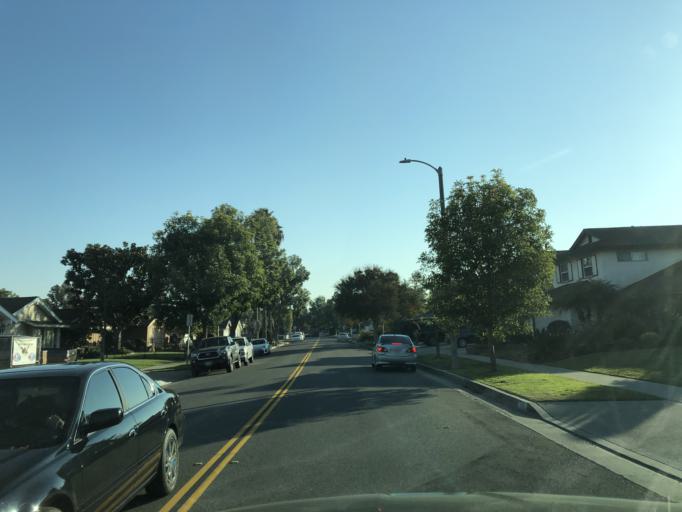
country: US
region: California
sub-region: Orange County
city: Tustin
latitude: 33.7629
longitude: -117.8441
